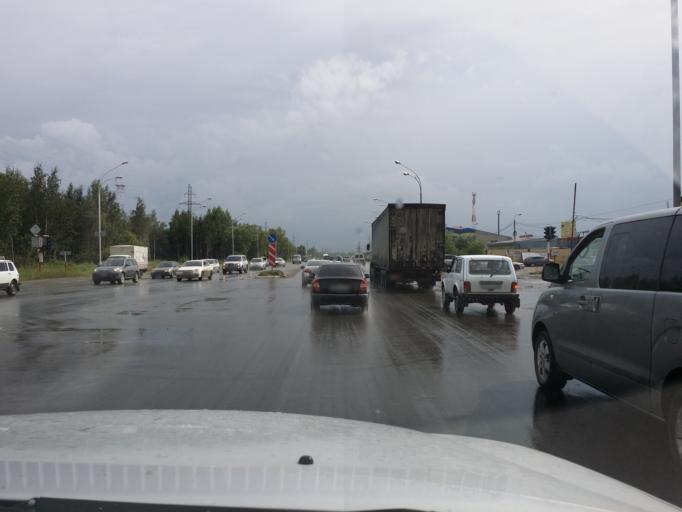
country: RU
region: Khanty-Mansiyskiy Avtonomnyy Okrug
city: Nizhnevartovsk
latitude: 60.9449
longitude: 76.5297
